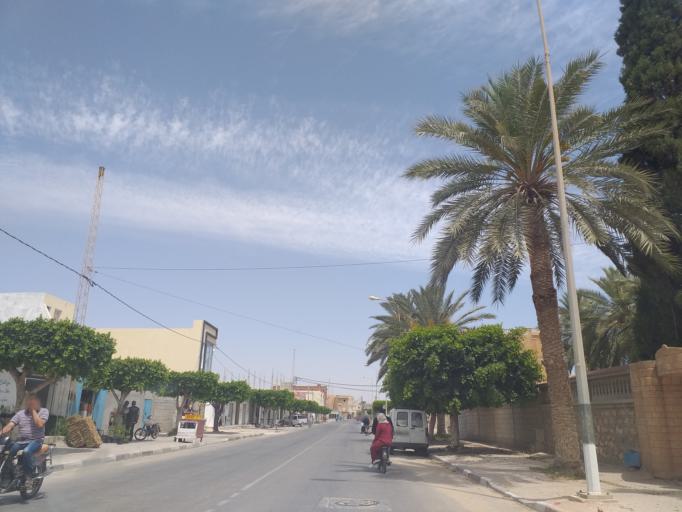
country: TN
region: Qabis
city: Gabes
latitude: 33.9339
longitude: 10.0706
